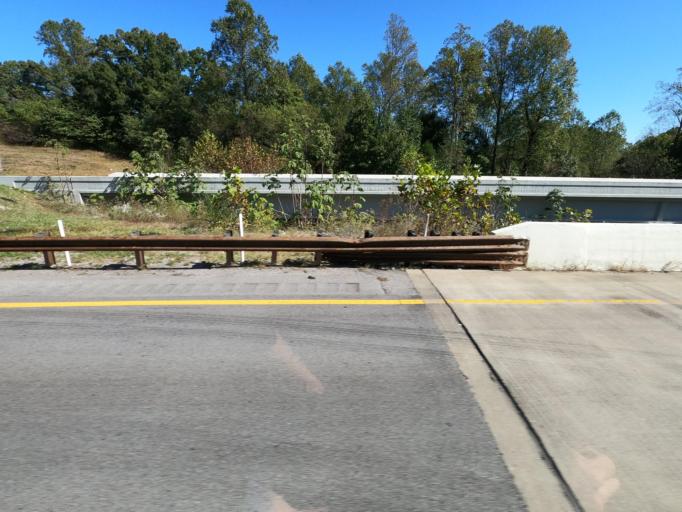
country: US
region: Tennessee
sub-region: Williamson County
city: Thompson's Station
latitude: 35.8190
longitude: -87.0356
